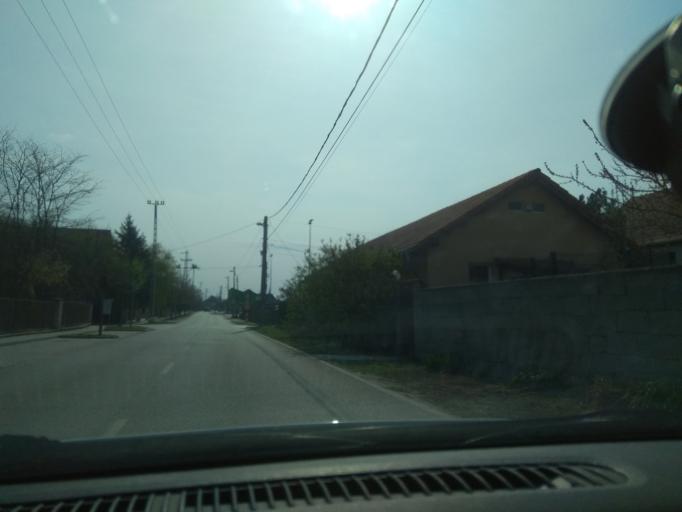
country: HU
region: Pest
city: Szigetszentmiklos
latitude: 47.3539
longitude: 19.0517
